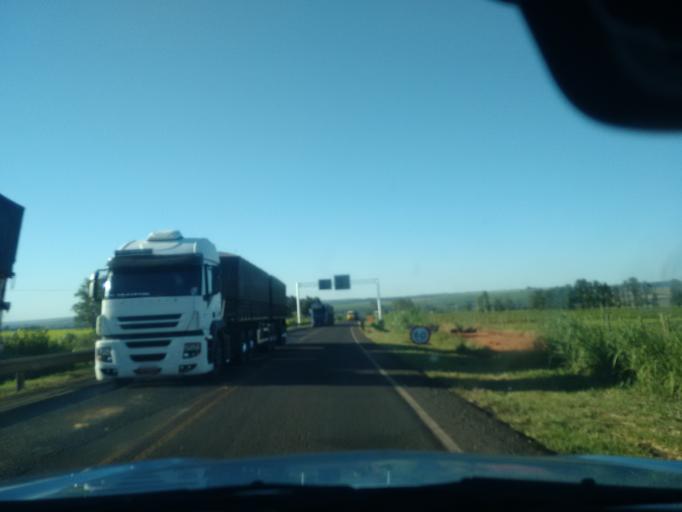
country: BR
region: Mato Grosso do Sul
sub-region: Eldorado
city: Eldorado
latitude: -23.8556
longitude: -54.3358
